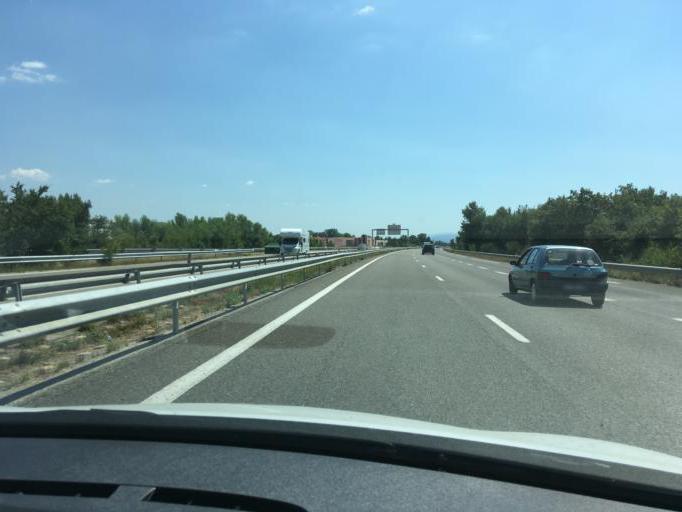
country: FR
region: Provence-Alpes-Cote d'Azur
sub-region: Departement des Alpes-de-Haute-Provence
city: Manosque
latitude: 43.8037
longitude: 5.8156
